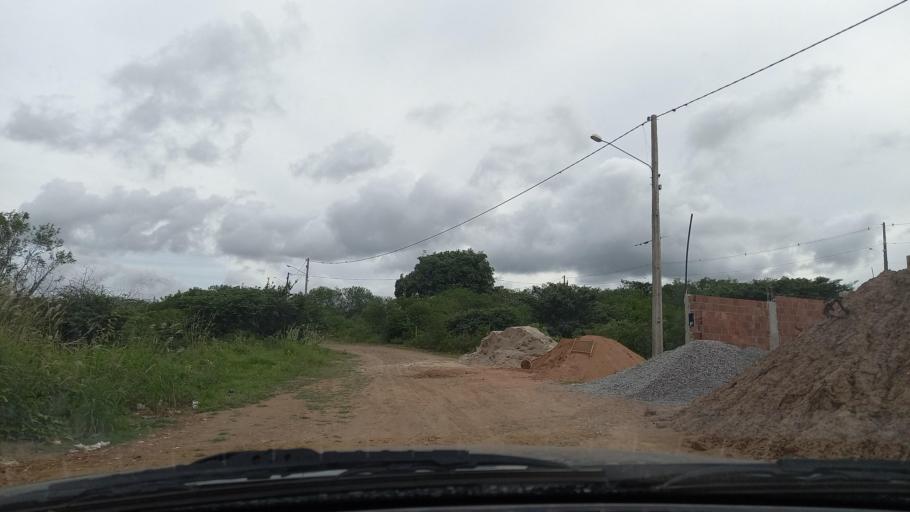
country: BR
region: Pernambuco
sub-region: Gravata
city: Gravata
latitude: -8.2247
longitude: -35.5733
